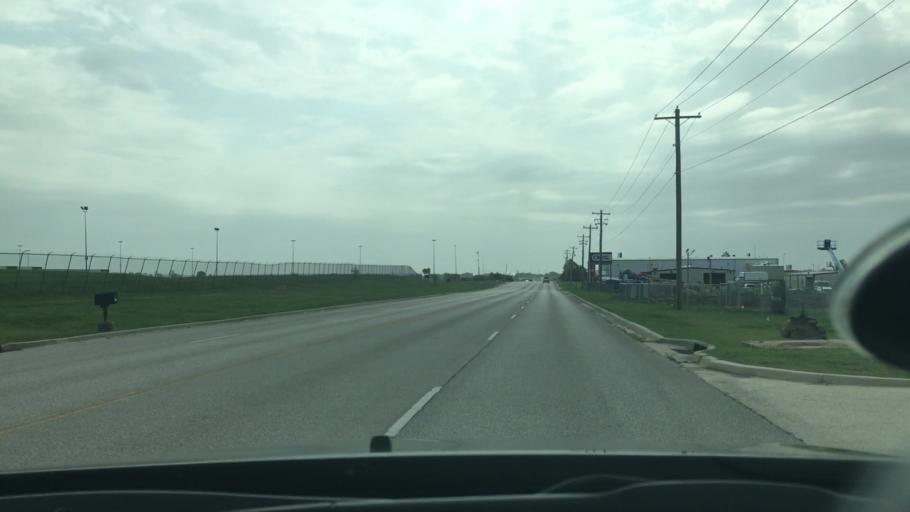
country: US
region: Oklahoma
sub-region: Carter County
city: Ardmore
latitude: 34.2019
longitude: -97.1731
